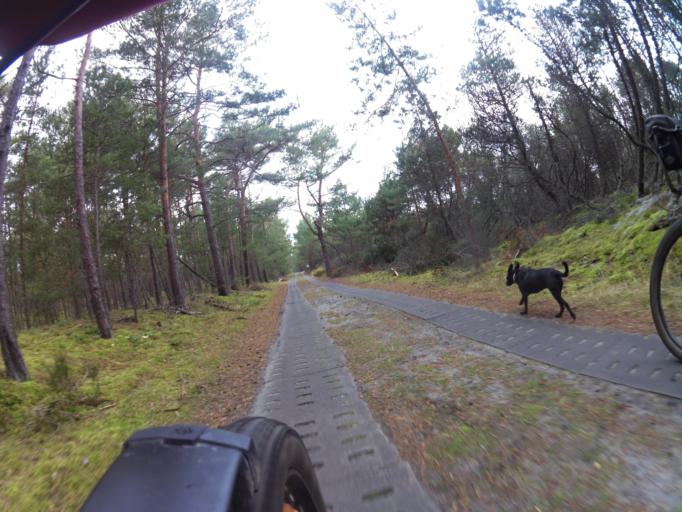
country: PL
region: Pomeranian Voivodeship
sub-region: Powiat pucki
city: Hel
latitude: 54.6220
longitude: 18.8196
